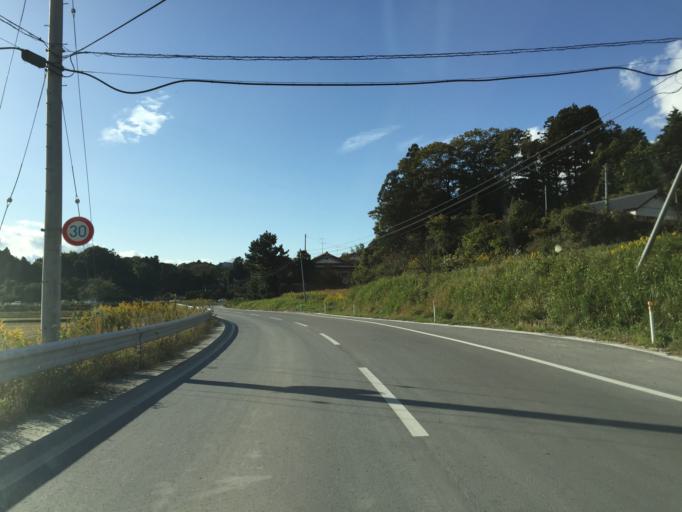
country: JP
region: Miyagi
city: Marumori
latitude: 37.8838
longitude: 140.9175
